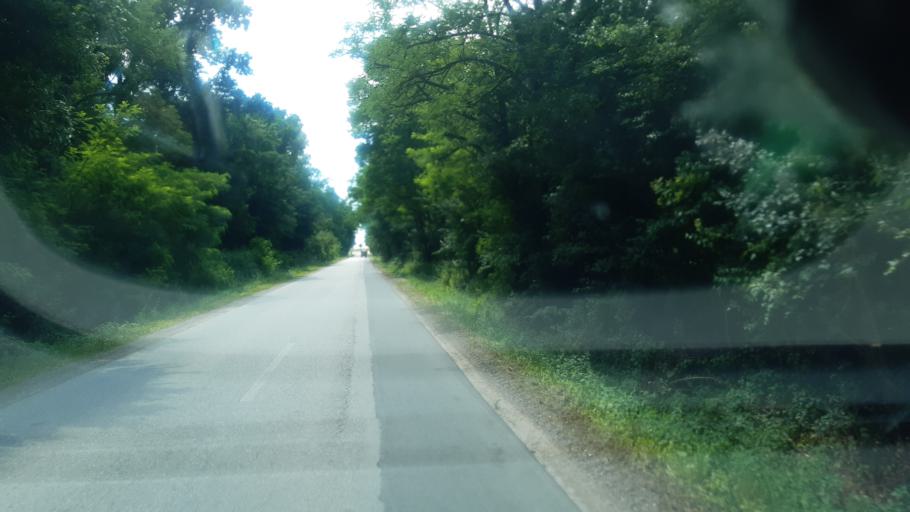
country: SI
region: Beltinci
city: Gancani
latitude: 46.6433
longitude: 16.2655
